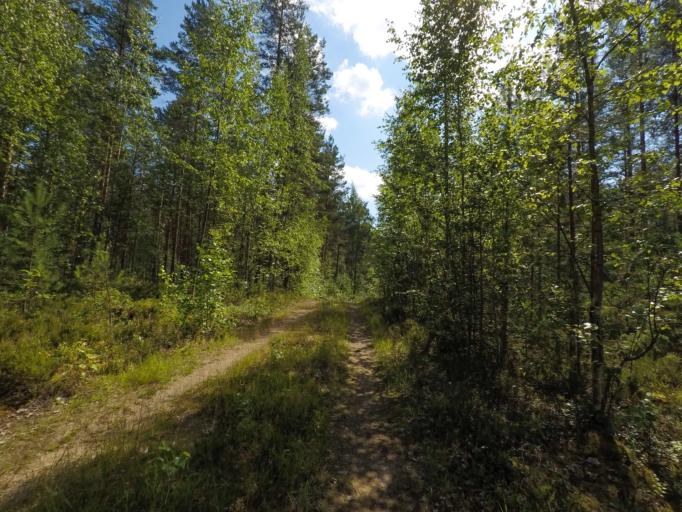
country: FI
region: Southern Savonia
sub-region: Mikkeli
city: Puumala
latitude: 61.5165
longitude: 28.1662
